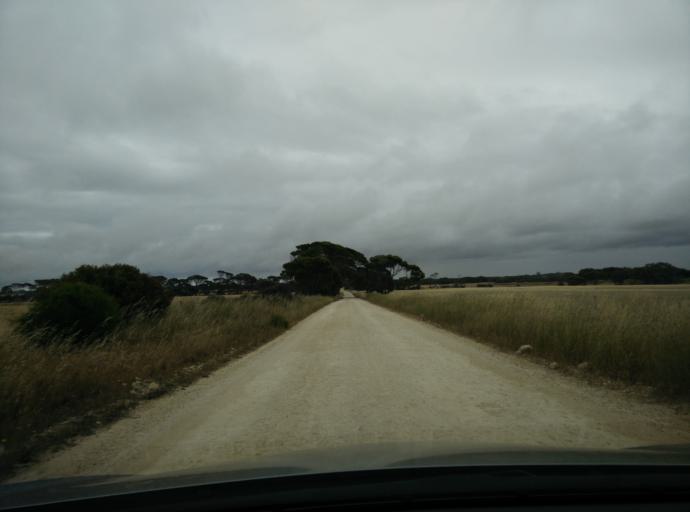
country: AU
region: South Australia
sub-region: Kangaroo Island
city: Kingscote
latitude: -35.8687
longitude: 137.5315
